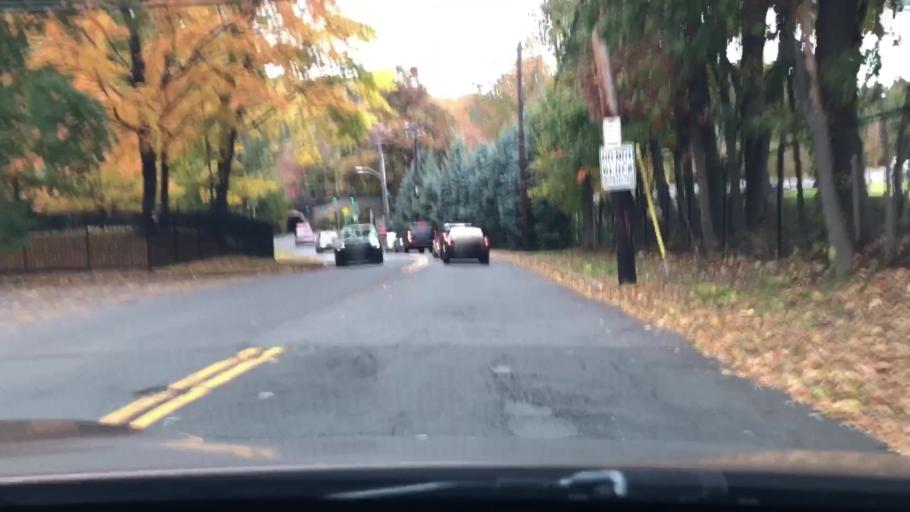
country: US
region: New York
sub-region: Westchester County
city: Tuckahoe
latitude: 40.9682
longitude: -73.8150
